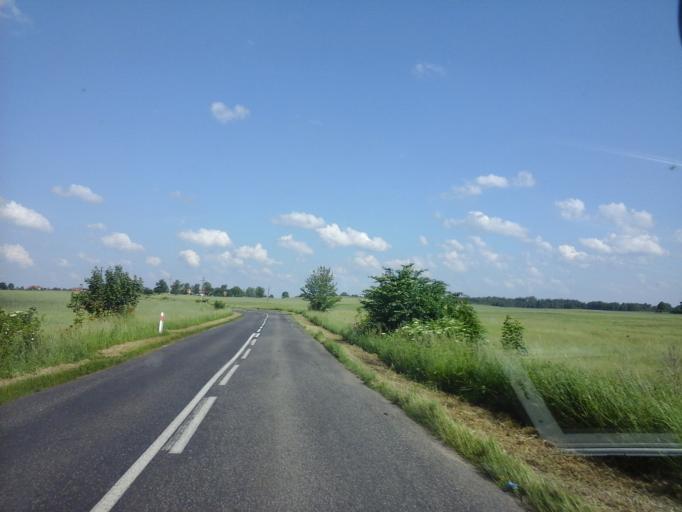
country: PL
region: Lubusz
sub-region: Powiat strzelecko-drezdenecki
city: Dobiegniew
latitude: 53.0019
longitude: 15.7442
